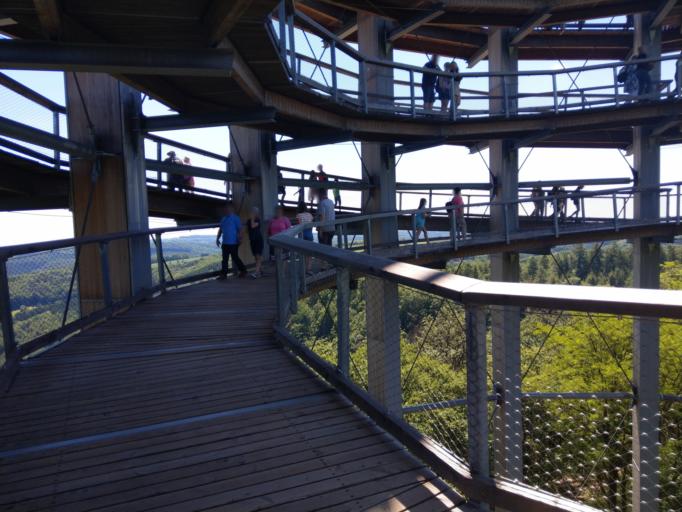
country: DE
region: Saarland
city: Orscholz
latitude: 49.5022
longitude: 6.5403
